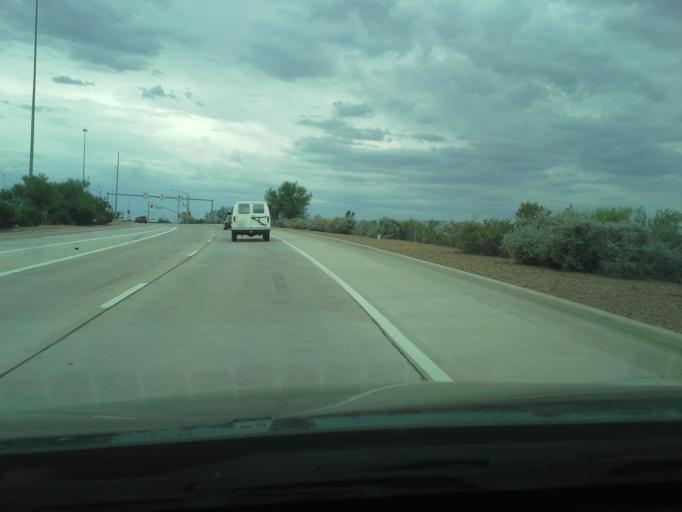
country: US
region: Arizona
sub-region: Pima County
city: Flowing Wells
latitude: 32.2612
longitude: -111.0050
